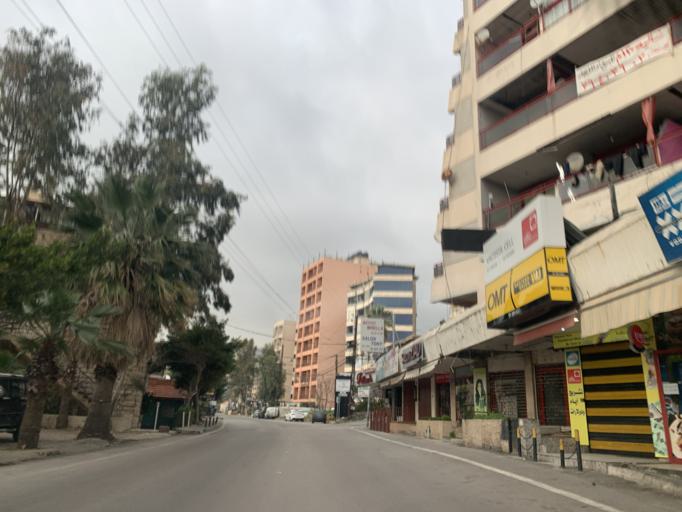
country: LB
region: Mont-Liban
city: Djounie
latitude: 34.0027
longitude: 35.6449
